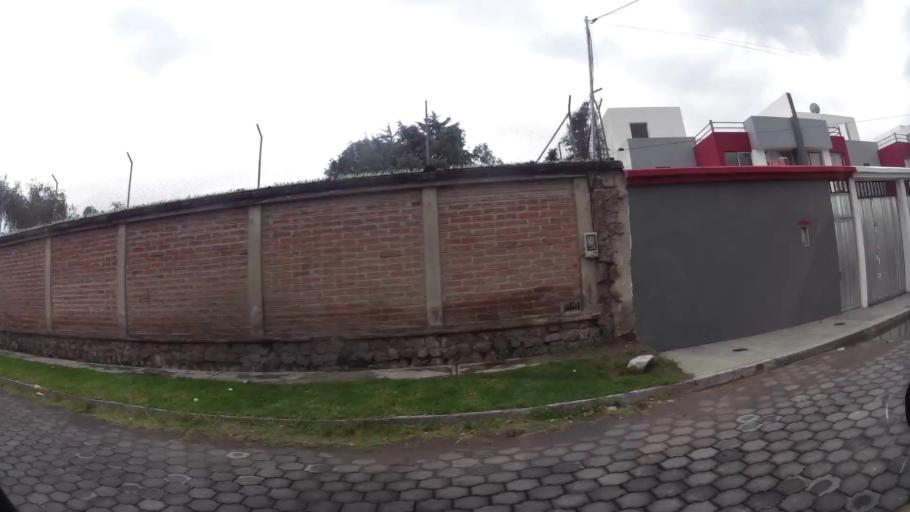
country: EC
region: Pichincha
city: Sangolqui
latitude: -0.3214
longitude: -78.4706
